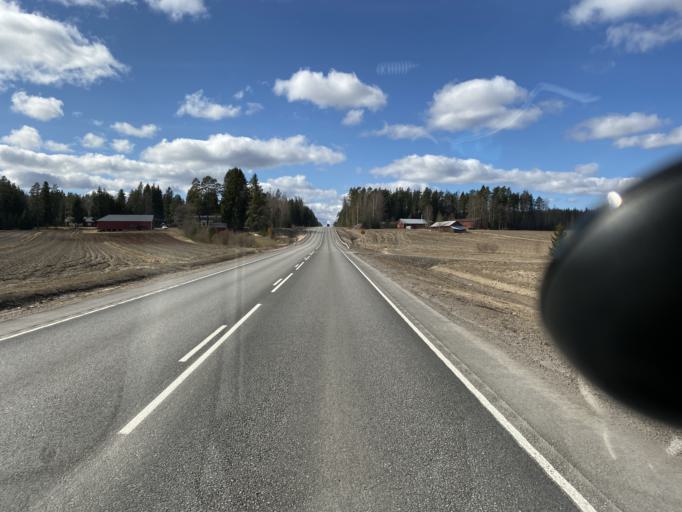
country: FI
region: Satakunta
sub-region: Rauma
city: Koeylioe
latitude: 61.1532
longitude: 22.2601
